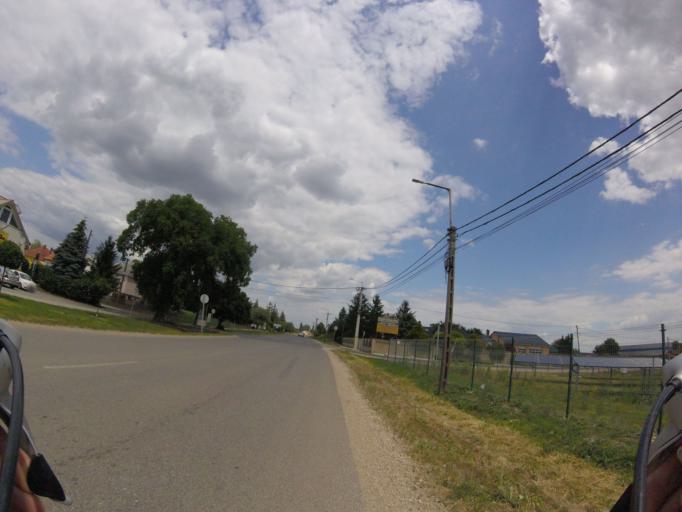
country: HU
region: Fejer
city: Seregelyes
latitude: 47.1099
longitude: 18.5855
